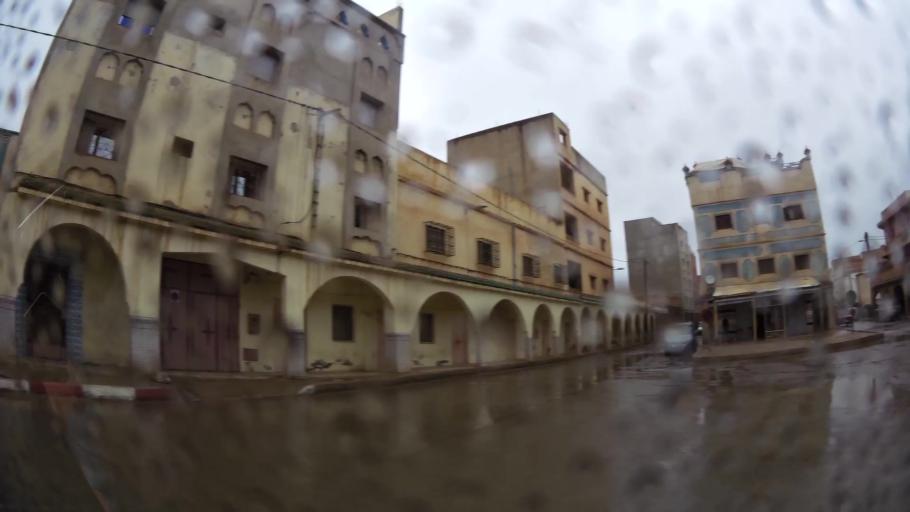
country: MA
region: Oriental
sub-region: Nador
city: Boudinar
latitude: 35.1183
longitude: -3.6409
